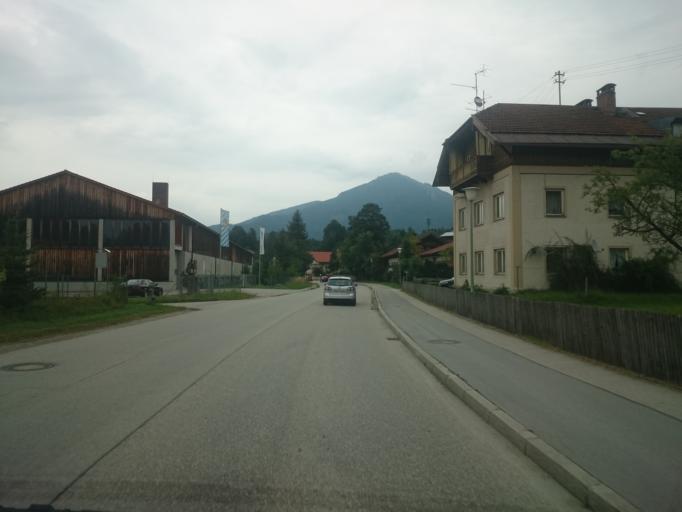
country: DE
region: Bavaria
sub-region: Upper Bavaria
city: Lenggries
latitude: 47.6488
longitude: 11.5880
